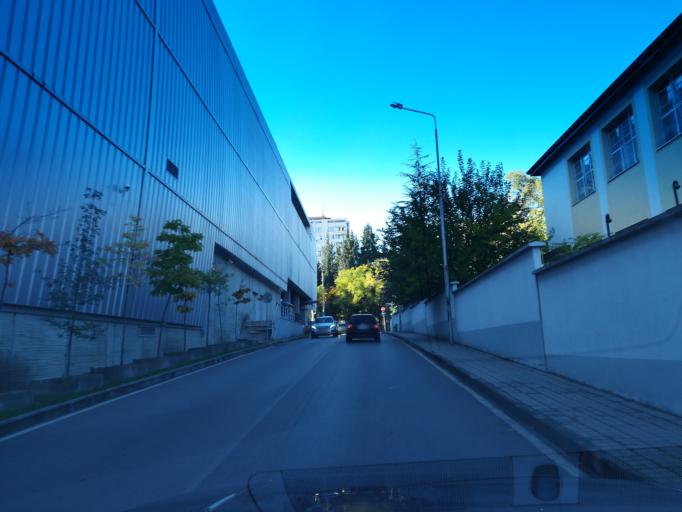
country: BG
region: Stara Zagora
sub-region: Obshtina Stara Zagora
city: Stara Zagora
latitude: 42.4384
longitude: 25.6330
